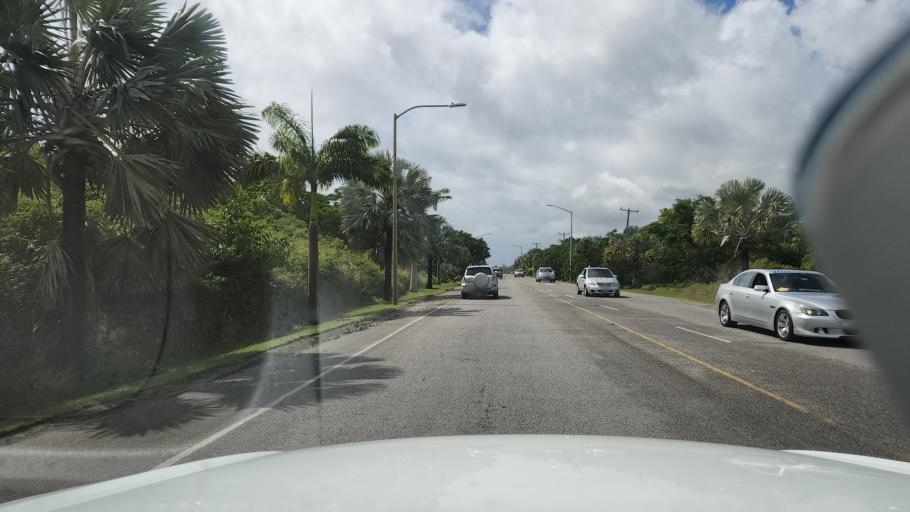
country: BB
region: Christ Church
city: Oistins
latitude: 13.0801
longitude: -59.5156
